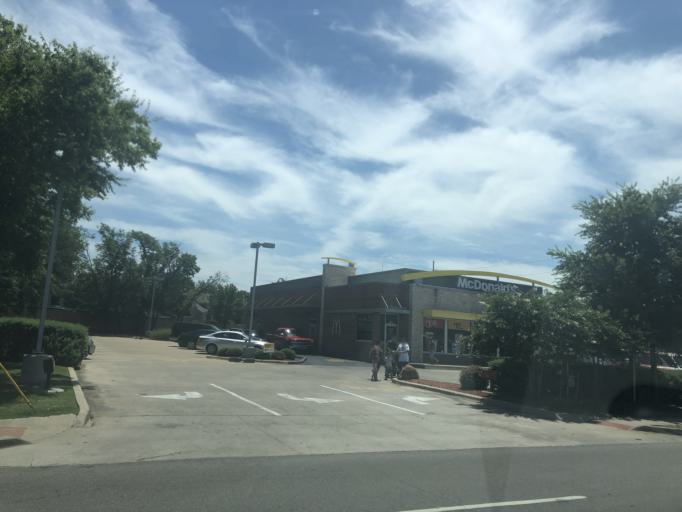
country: US
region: Texas
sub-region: Dallas County
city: Dallas
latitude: 32.7797
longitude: -96.8565
